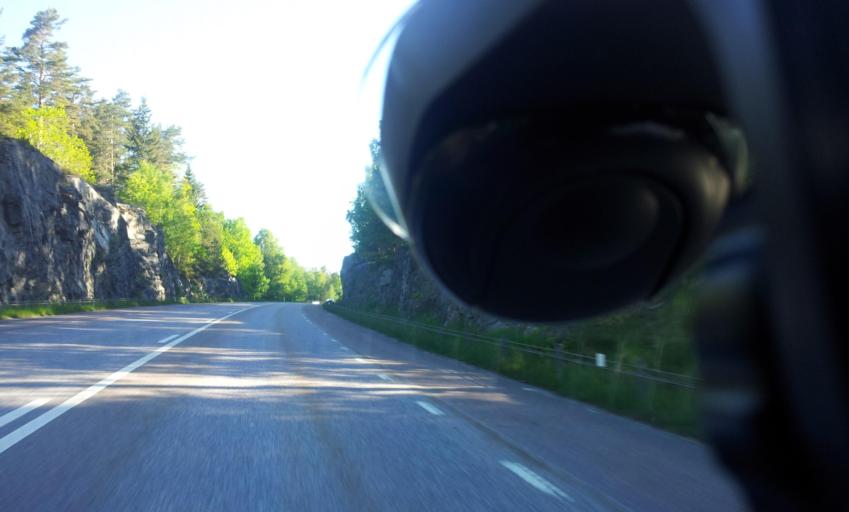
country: SE
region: Kalmar
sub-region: Vasterviks Kommun
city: Ankarsrum
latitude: 57.6671
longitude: 16.4416
